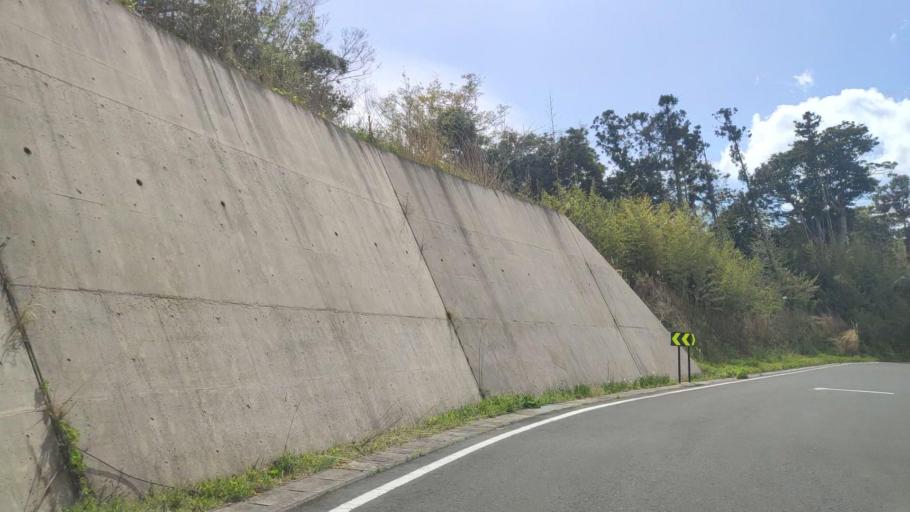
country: JP
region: Miyagi
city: Yamoto
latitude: 38.3363
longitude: 141.1666
